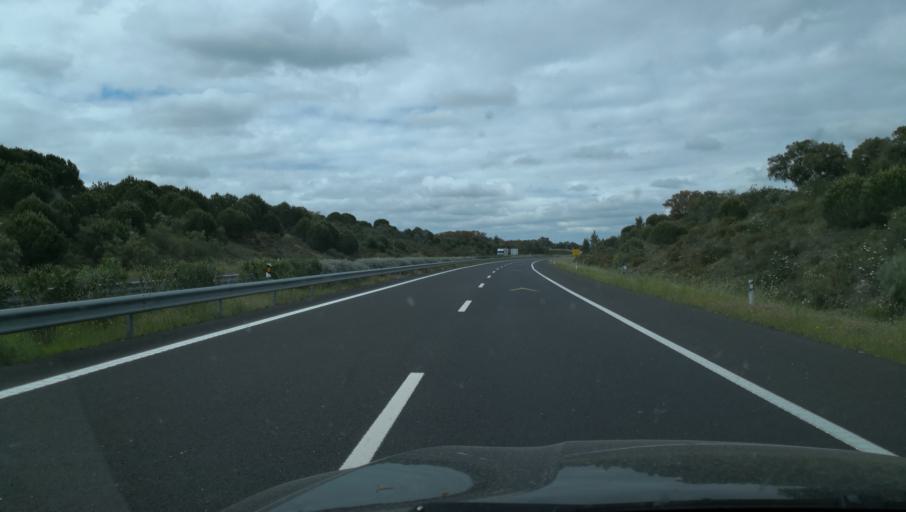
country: PT
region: Santarem
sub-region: Benavente
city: Poceirao
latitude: 38.8791
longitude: -8.7938
